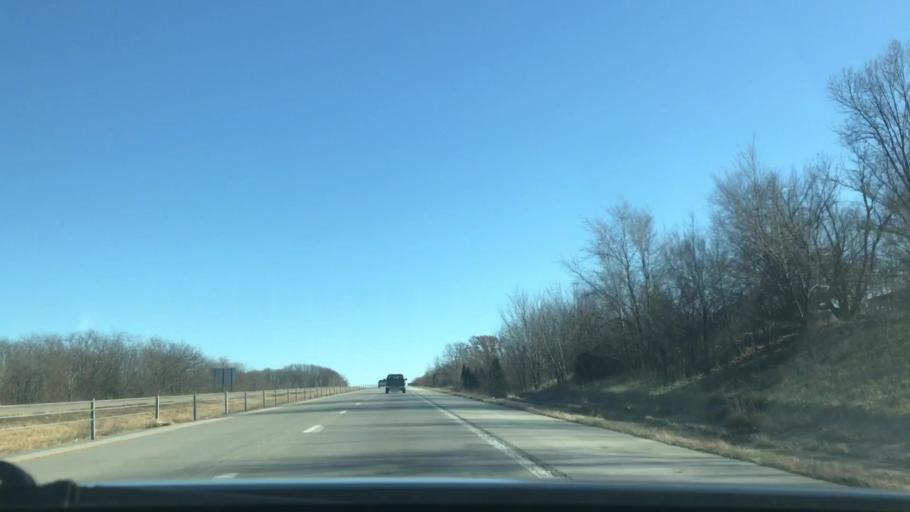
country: US
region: Missouri
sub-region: Platte County
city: Weatherby Lake
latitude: 39.2540
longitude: -94.7090
